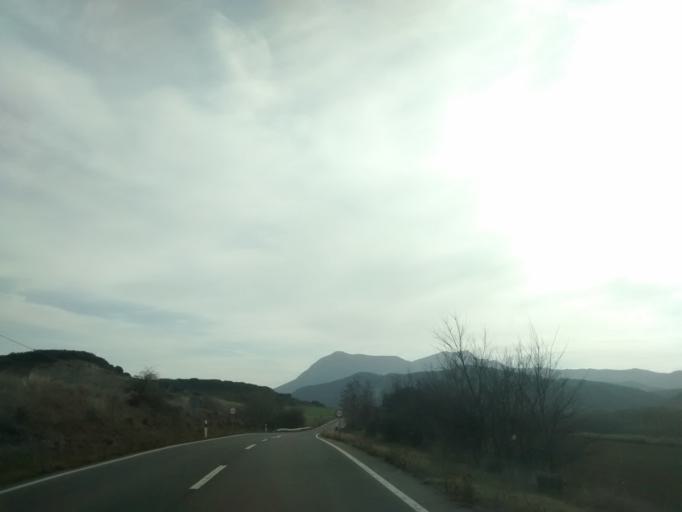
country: ES
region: Aragon
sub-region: Provincia de Huesca
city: Bailo
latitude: 42.5689
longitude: -0.8095
